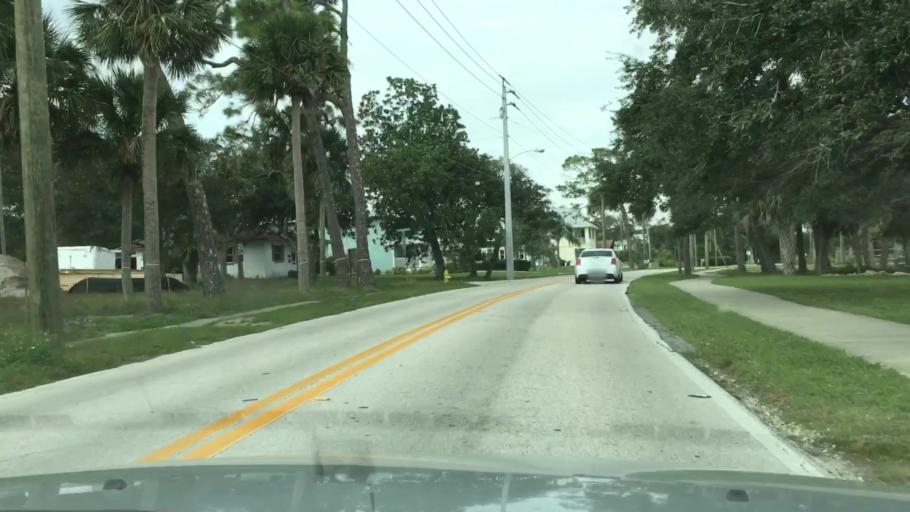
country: US
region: Florida
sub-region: Volusia County
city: Ormond Beach
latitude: 29.2785
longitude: -81.0524
